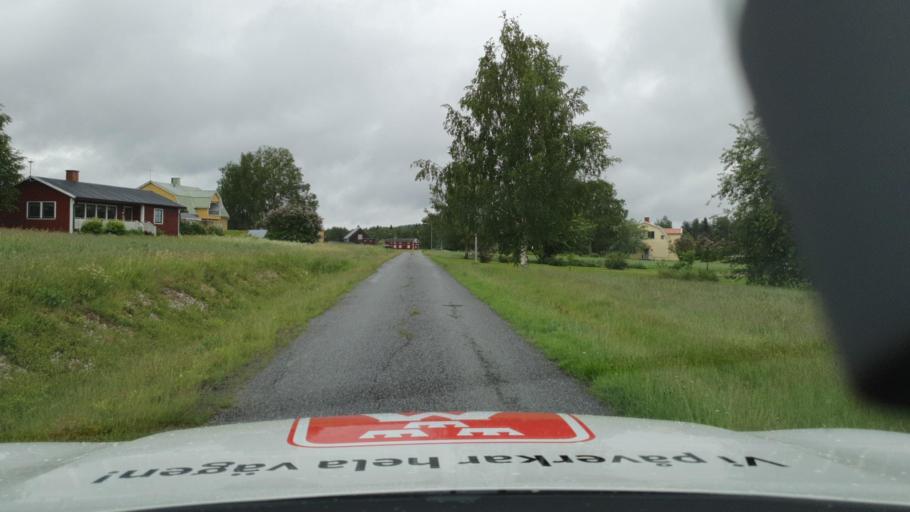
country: SE
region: Vaesterbotten
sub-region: Asele Kommun
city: Asele
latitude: 63.9422
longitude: 17.2686
